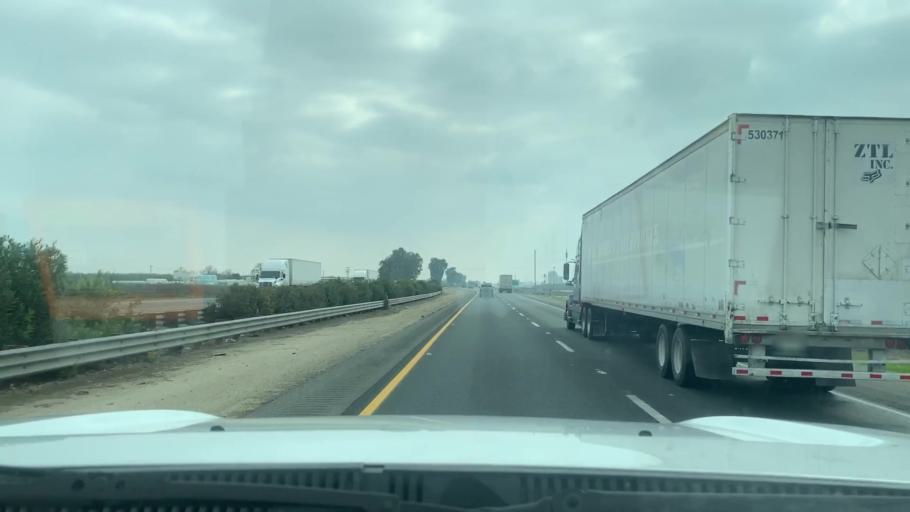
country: US
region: California
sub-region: Tulare County
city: Tipton
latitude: 36.0265
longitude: -119.3070
